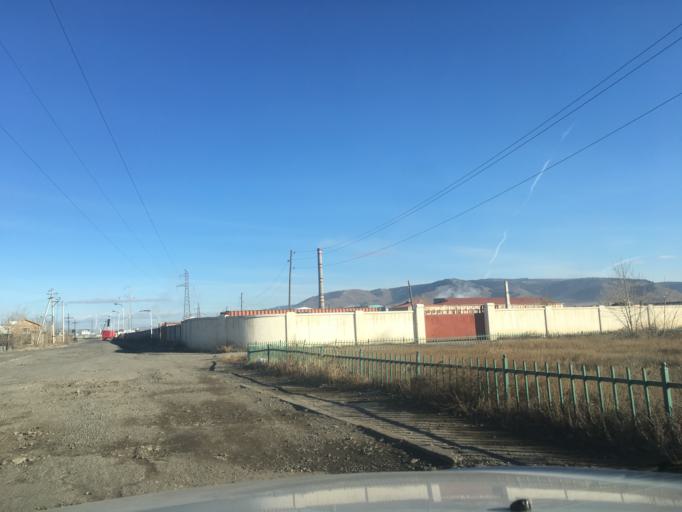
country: MN
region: Ulaanbaatar
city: Ulaanbaatar
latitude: 47.9015
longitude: 106.7814
